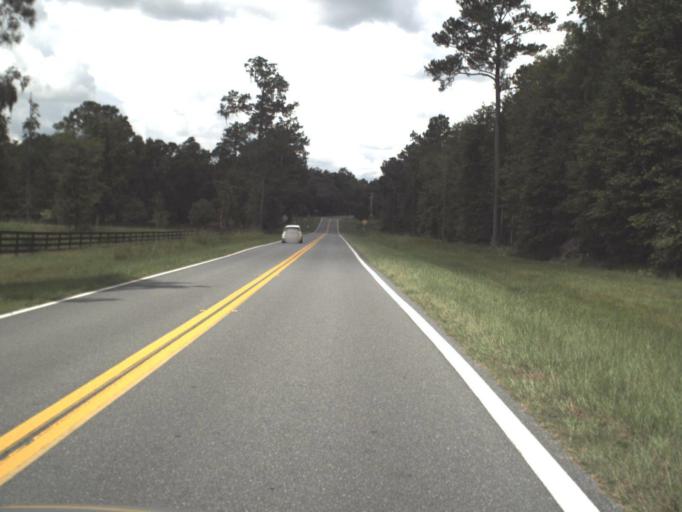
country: US
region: Florida
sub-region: Union County
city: Lake Butler
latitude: 29.9318
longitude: -82.4176
